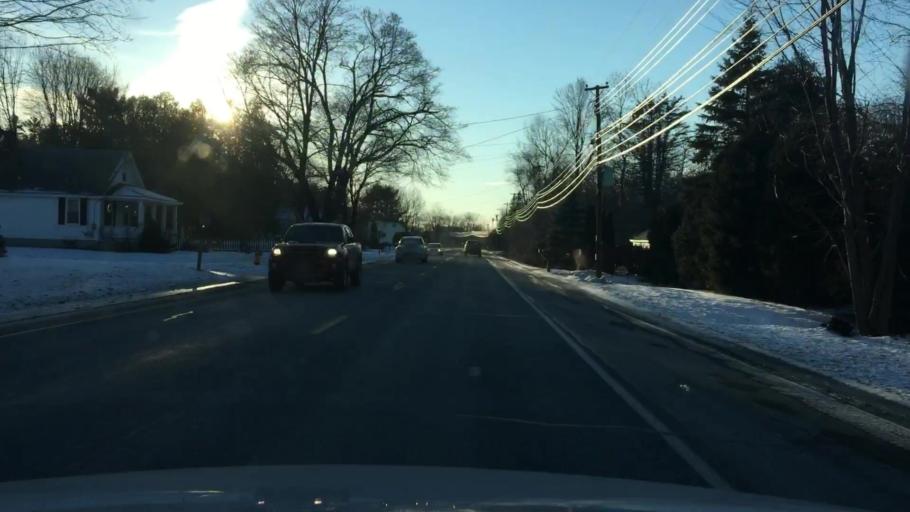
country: US
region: Maine
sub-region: Penobscot County
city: Veazie
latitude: 44.8173
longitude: -68.7239
